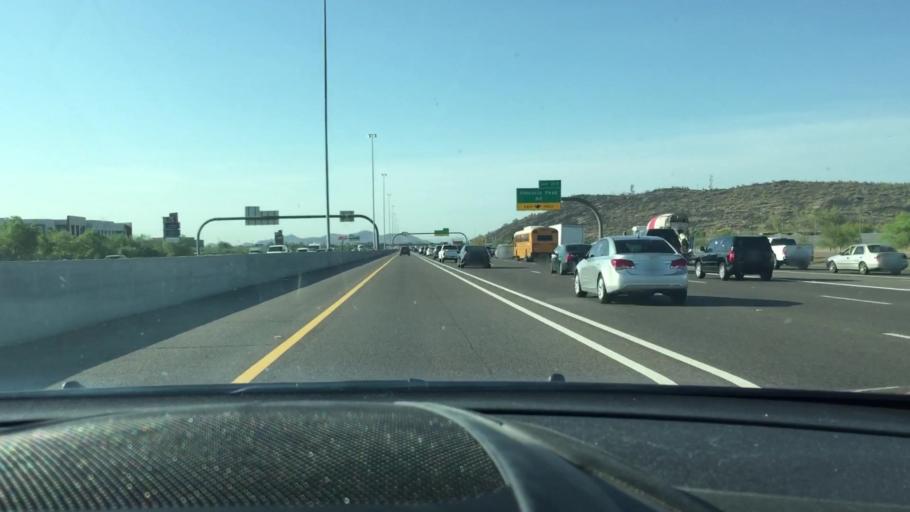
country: US
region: Arizona
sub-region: Maricopa County
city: Anthem
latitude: 33.7083
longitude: -112.1151
